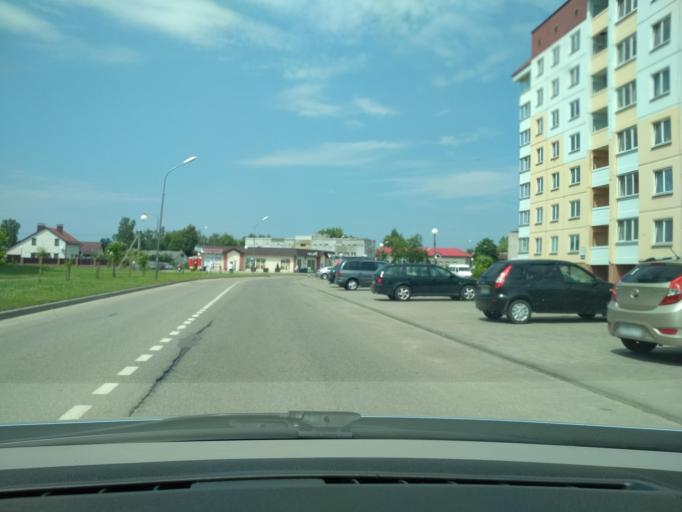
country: BY
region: Grodnenskaya
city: Astravyets
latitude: 54.6084
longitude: 25.9682
